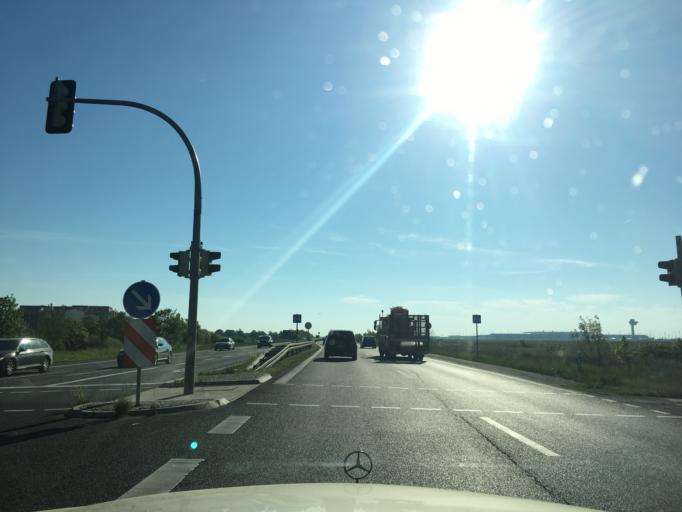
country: DE
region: Brandenburg
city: Schonefeld
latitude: 52.3673
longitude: 13.4669
